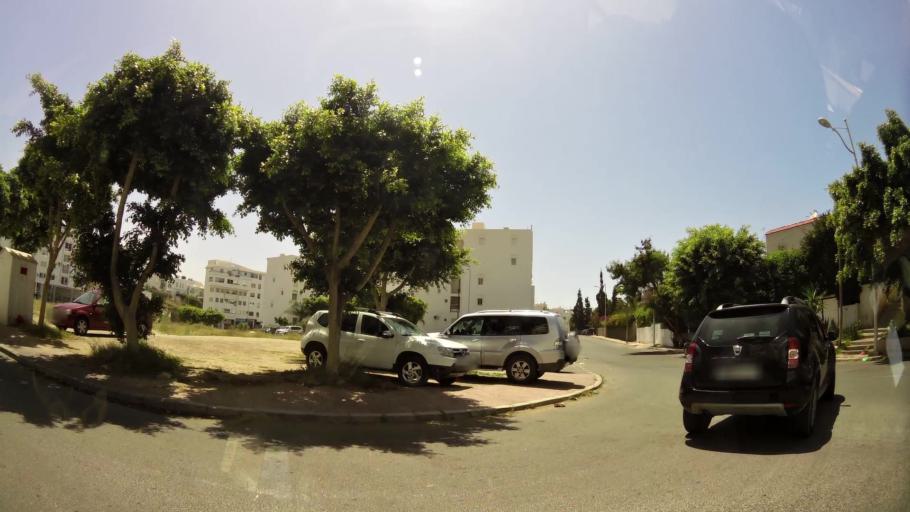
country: MA
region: Souss-Massa-Draa
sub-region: Agadir-Ida-ou-Tnan
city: Agadir
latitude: 30.4316
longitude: -9.5869
